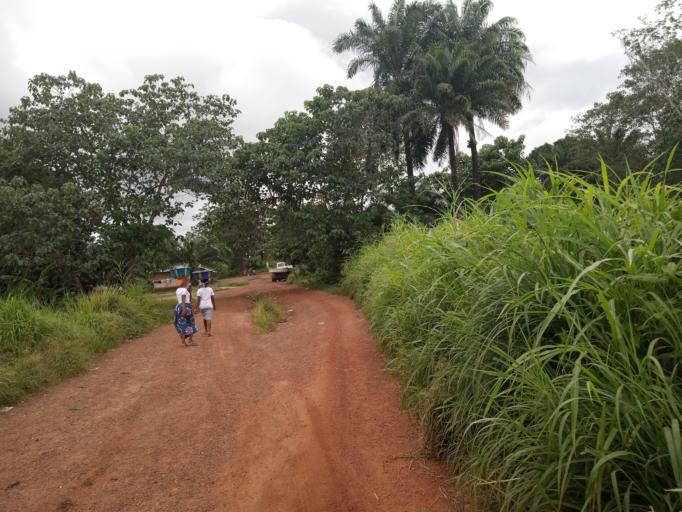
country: SL
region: Northern Province
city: Kamakwie
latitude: 9.4900
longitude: -12.2454
